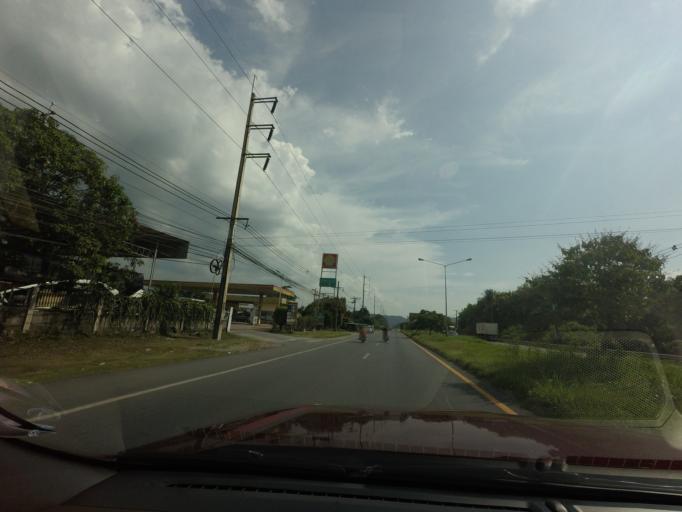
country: TH
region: Yala
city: Yala
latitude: 6.5515
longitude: 101.2587
